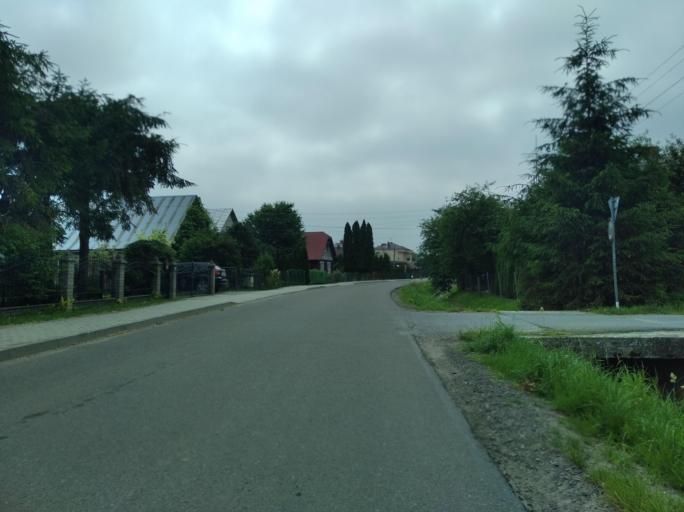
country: PL
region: Subcarpathian Voivodeship
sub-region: Powiat sanocki
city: Besko
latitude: 49.5927
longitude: 21.9402
